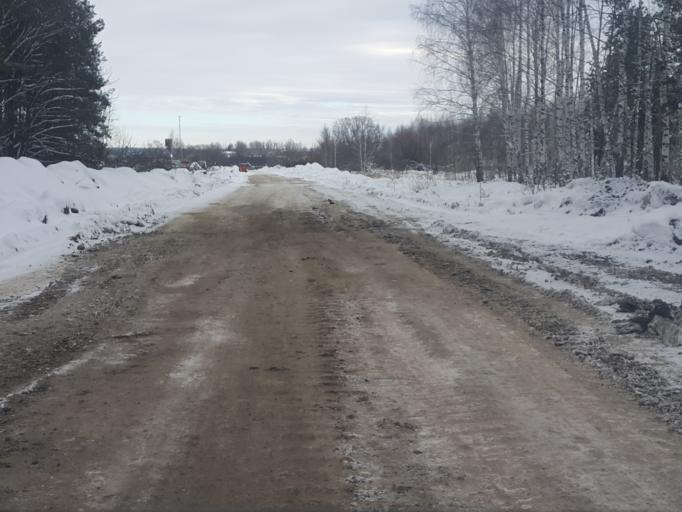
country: RU
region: Tambov
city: Platonovka
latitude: 52.8821
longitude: 41.8691
